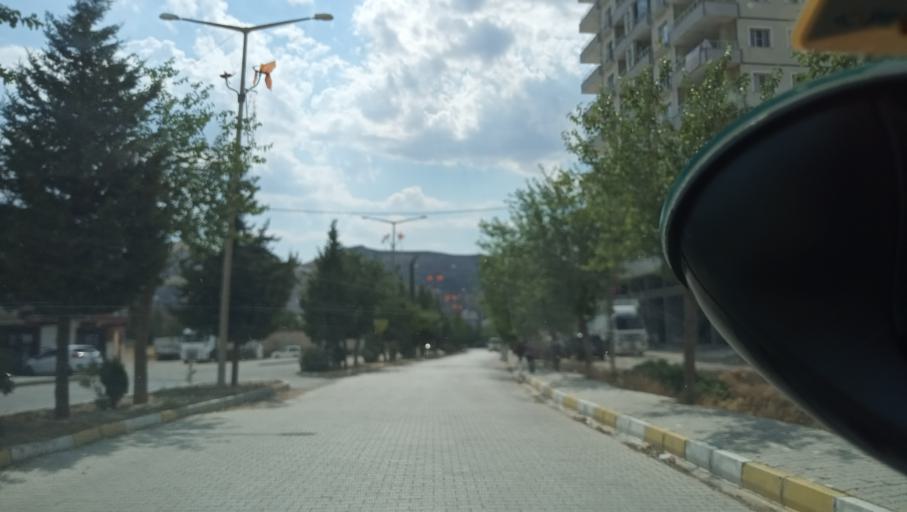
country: TR
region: Mardin
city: Kabala
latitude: 37.3401
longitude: 40.8138
